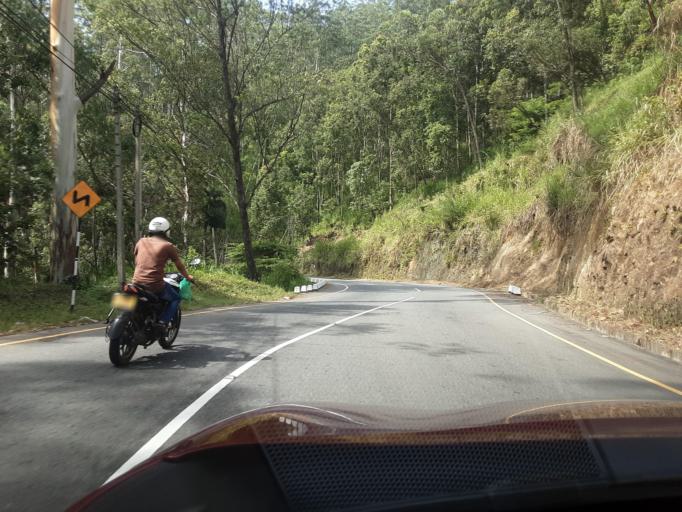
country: LK
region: Uva
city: Badulla
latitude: 6.9647
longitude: 81.0942
